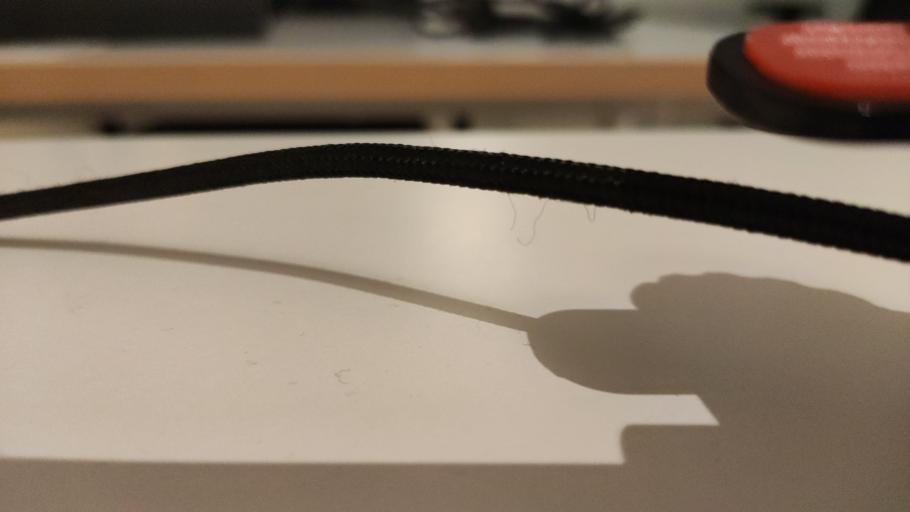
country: RU
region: Moskovskaya
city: Novoye
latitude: 55.6421
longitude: 38.9291
